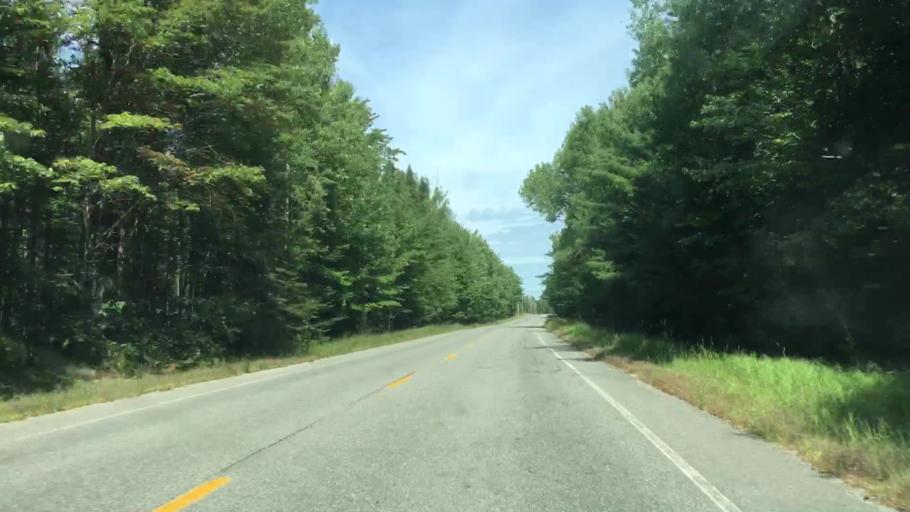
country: US
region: Maine
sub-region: Penobscot County
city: Lincoln
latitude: 45.3872
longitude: -68.5375
